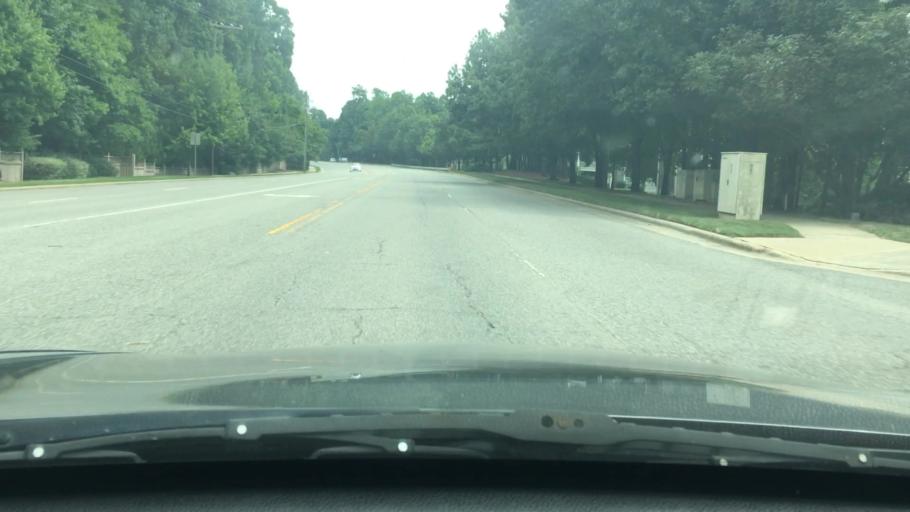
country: US
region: North Carolina
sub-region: Wake County
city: West Raleigh
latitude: 35.8371
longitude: -78.7135
